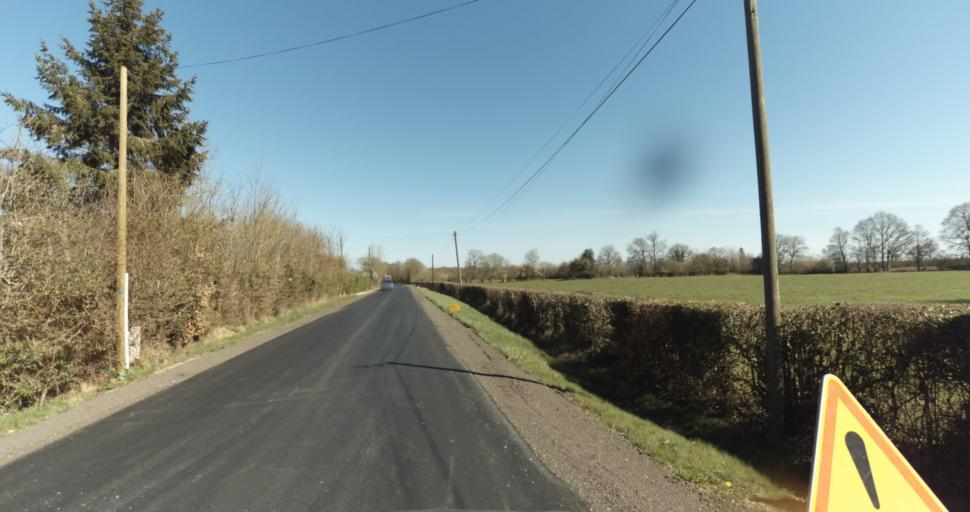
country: FR
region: Lower Normandy
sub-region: Departement du Calvados
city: Livarot
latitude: 48.9401
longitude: 0.0824
